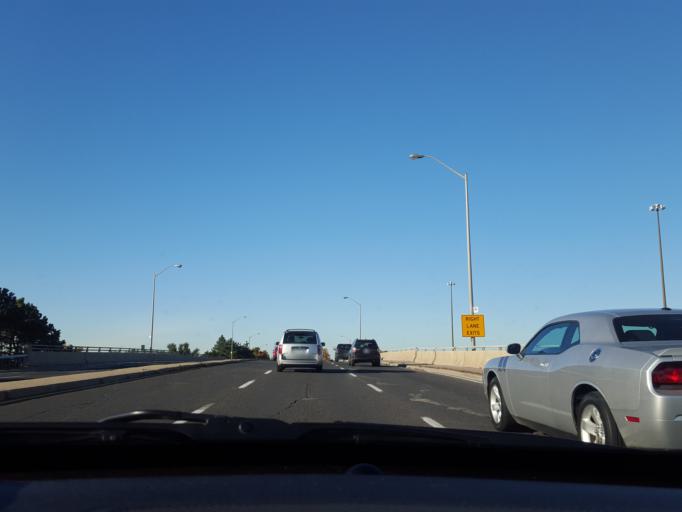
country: CA
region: Ontario
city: Scarborough
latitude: 43.7781
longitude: -79.2642
